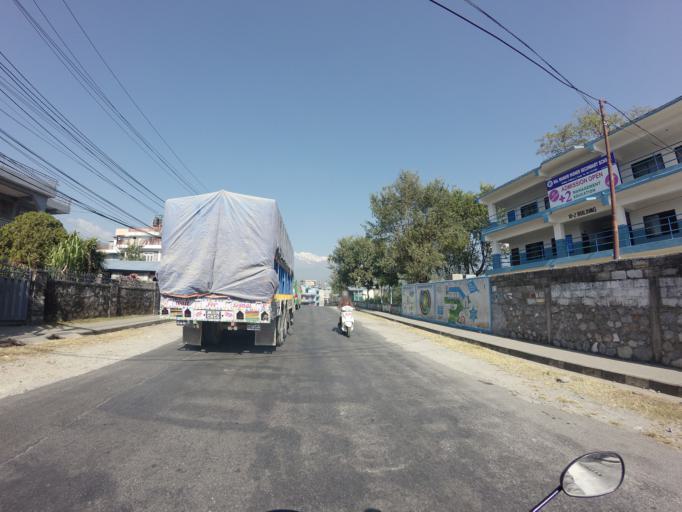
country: NP
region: Western Region
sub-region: Gandaki Zone
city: Pokhara
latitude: 28.2344
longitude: 83.9901
